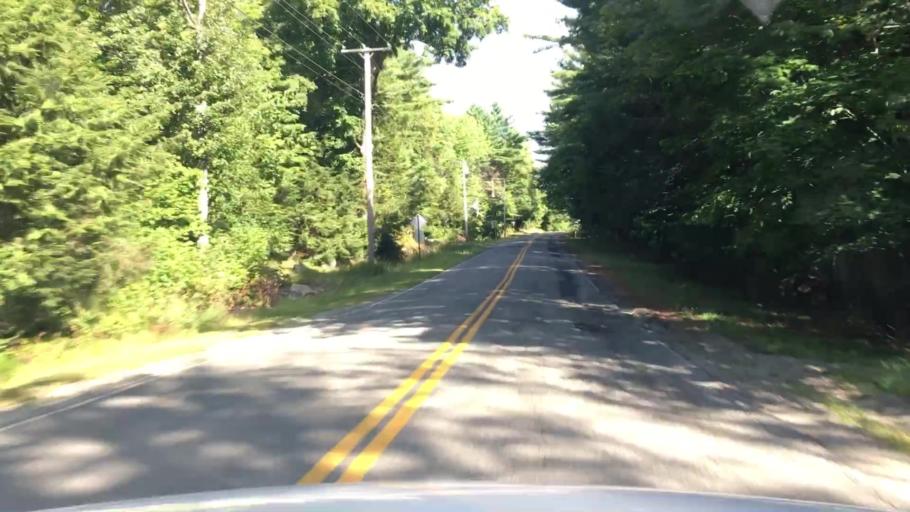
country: US
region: Maine
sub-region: Penobscot County
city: Enfield
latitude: 45.2406
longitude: -68.5628
